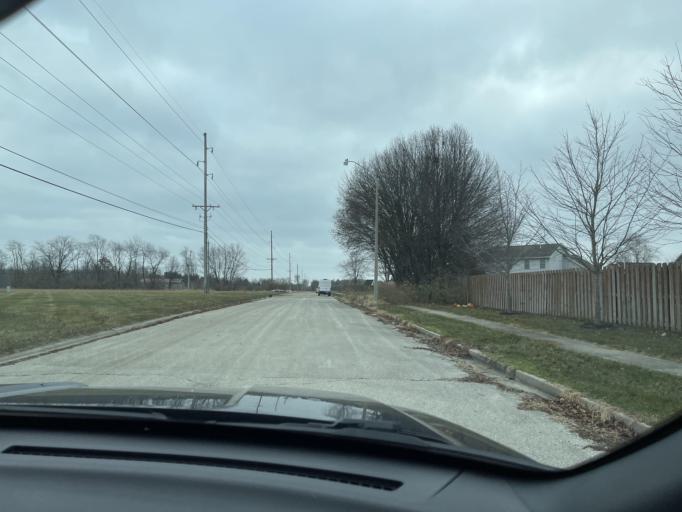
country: US
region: Illinois
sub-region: Sangamon County
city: Rochester
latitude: 39.7523
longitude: -89.5787
